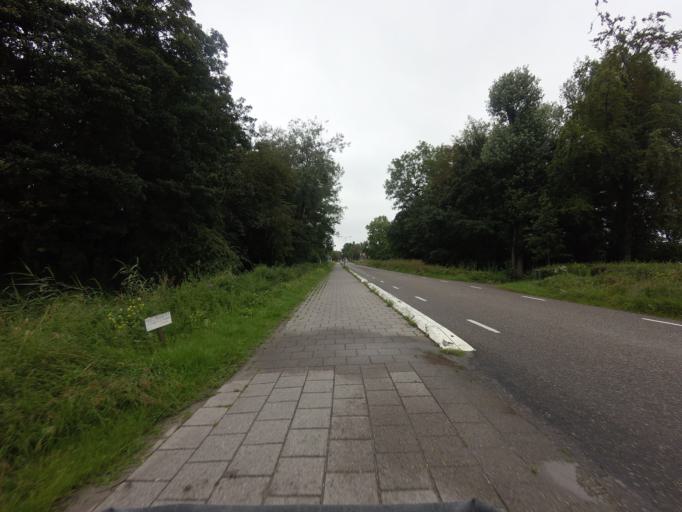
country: NL
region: North Holland
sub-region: Gemeente Opmeer
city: Opmeer
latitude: 52.7658
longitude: 4.8878
